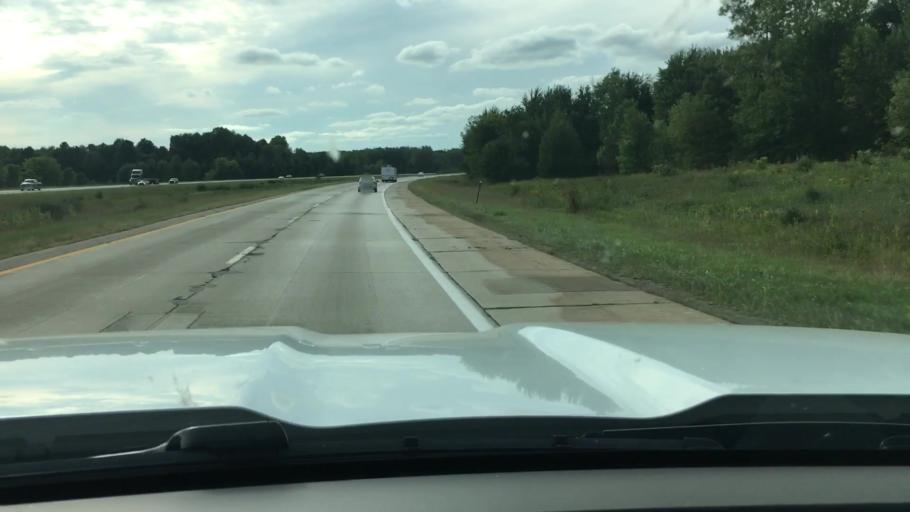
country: US
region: Michigan
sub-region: Lapeer County
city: Imlay City
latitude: 42.9966
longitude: -83.1309
